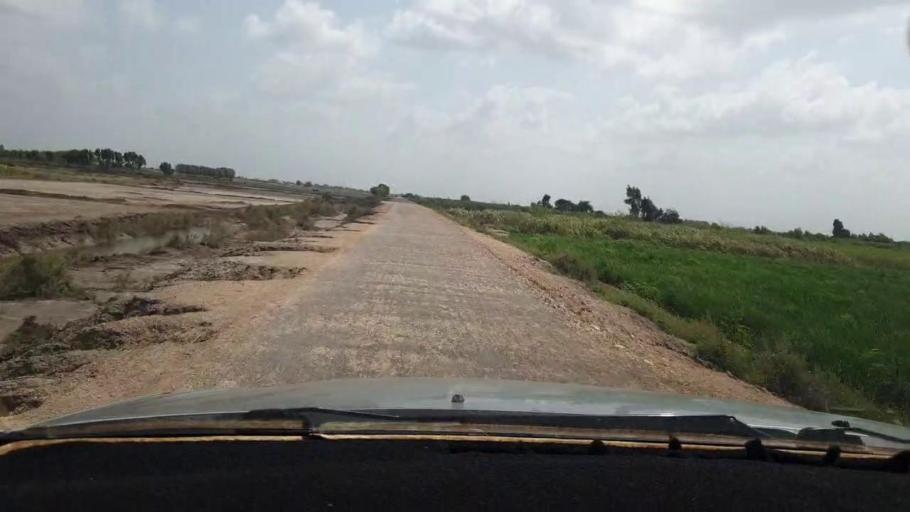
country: PK
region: Sindh
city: Tando Bago
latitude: 24.7207
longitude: 69.1754
